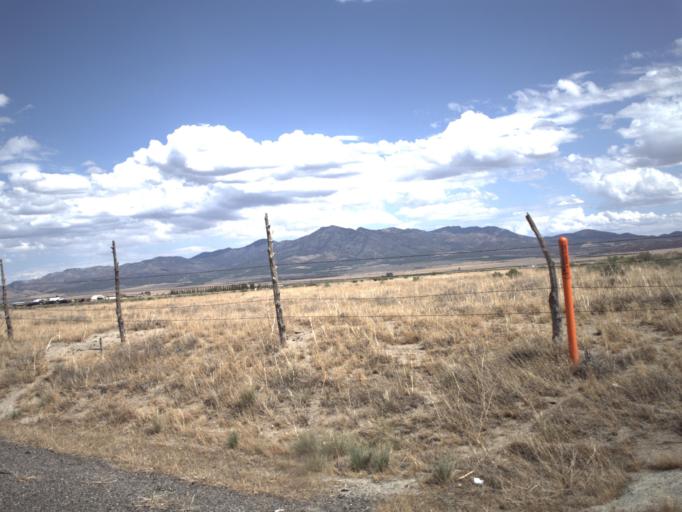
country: US
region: Utah
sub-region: Millard County
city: Fillmore
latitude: 39.1626
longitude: -112.4100
